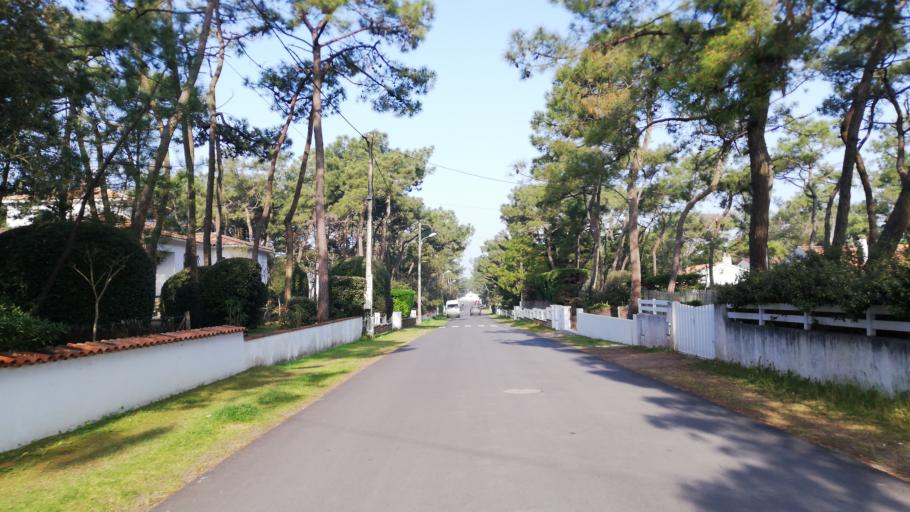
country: FR
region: Pays de la Loire
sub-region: Departement de la Vendee
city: La Tranche-sur-Mer
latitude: 46.3465
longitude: -1.4133
